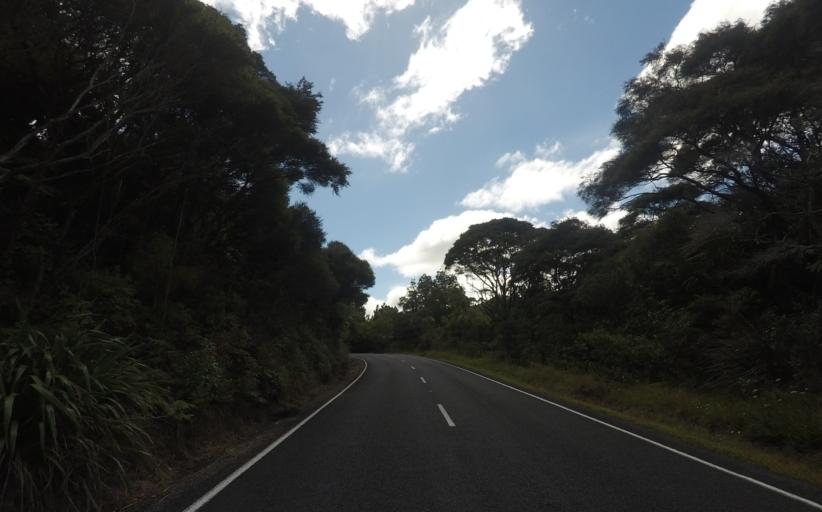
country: NZ
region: Auckland
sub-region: Auckland
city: Muriwai Beach
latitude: -36.8618
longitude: 174.5175
